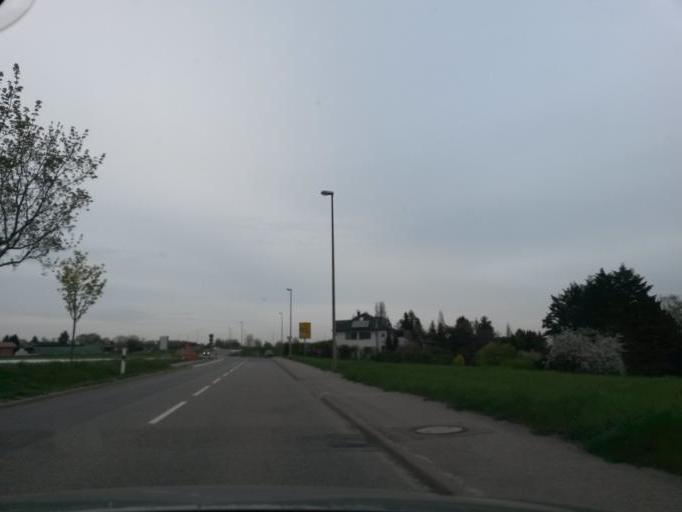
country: DE
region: Baden-Wuerttemberg
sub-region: Karlsruhe Region
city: Birkenfeld
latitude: 48.8813
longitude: 8.6316
